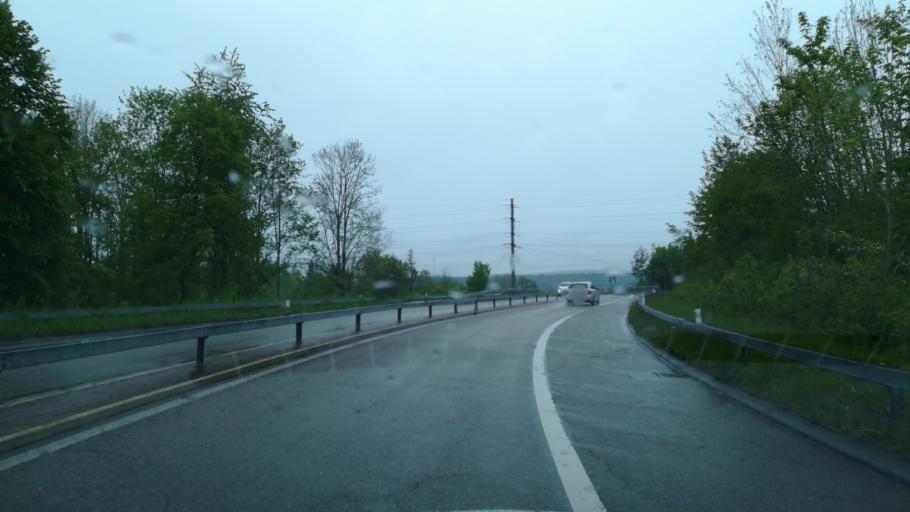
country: CH
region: Thurgau
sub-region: Frauenfeld District
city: Mullheim
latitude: 47.5882
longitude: 9.0006
